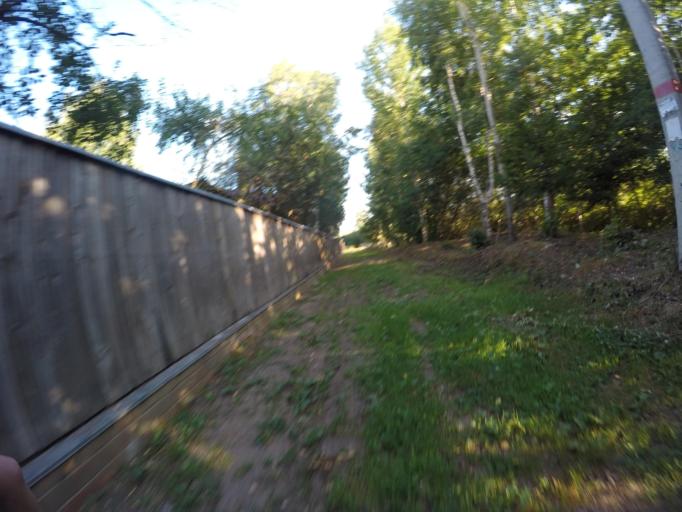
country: RU
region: Moskovskaya
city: Rechitsy
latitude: 55.5961
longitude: 38.4933
